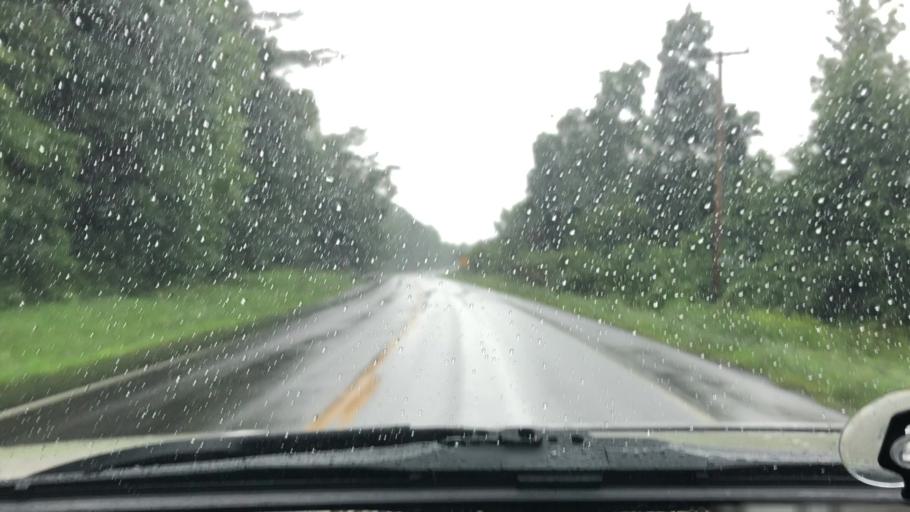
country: US
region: New York
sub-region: Greene County
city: Palenville
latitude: 42.2083
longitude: -73.9834
